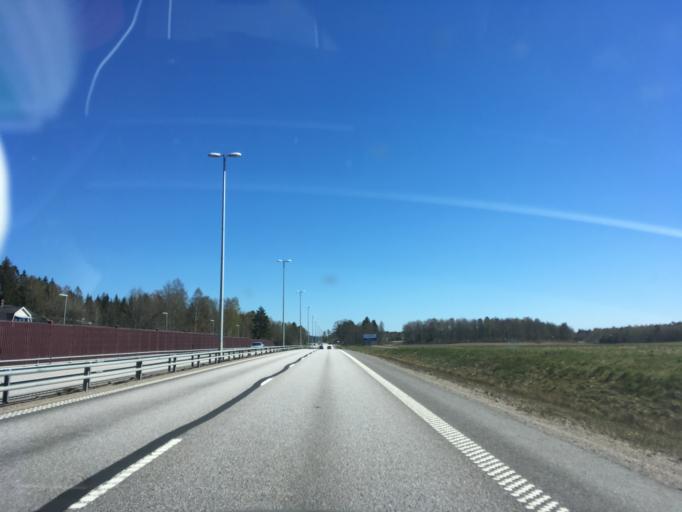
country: SE
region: Vaestra Goetaland
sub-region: Trollhattan
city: Trollhattan
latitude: 58.2463
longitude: 12.2642
